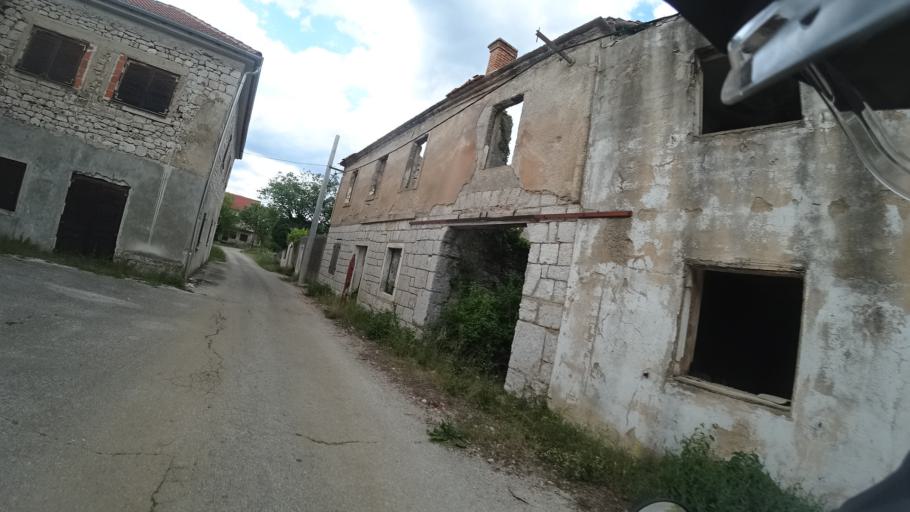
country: HR
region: Sibensko-Kniniska
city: Kistanje
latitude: 44.1082
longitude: 15.9402
